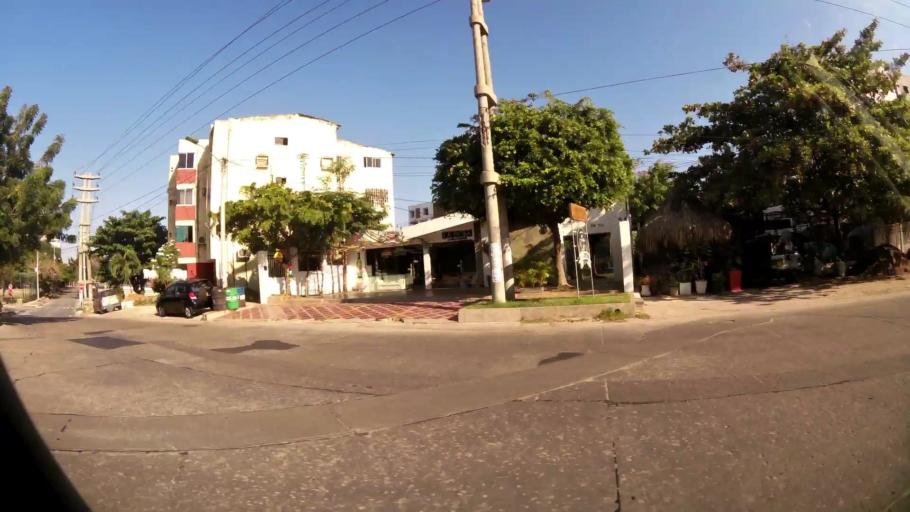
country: CO
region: Atlantico
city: Barranquilla
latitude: 11.0118
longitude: -74.8103
